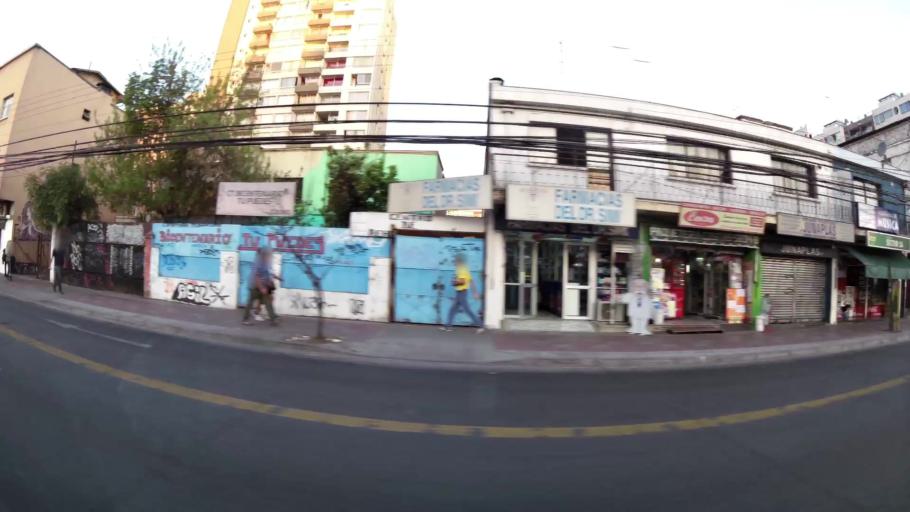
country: CL
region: Santiago Metropolitan
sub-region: Provincia de Santiago
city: Santiago
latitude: -33.5078
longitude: -70.6561
